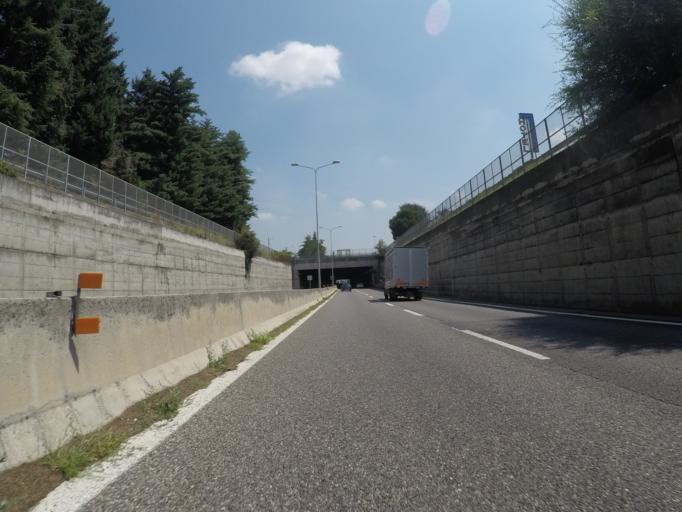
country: IT
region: Lombardy
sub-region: Provincia di Varese
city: Cardano al Campo
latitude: 45.6434
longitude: 8.7666
